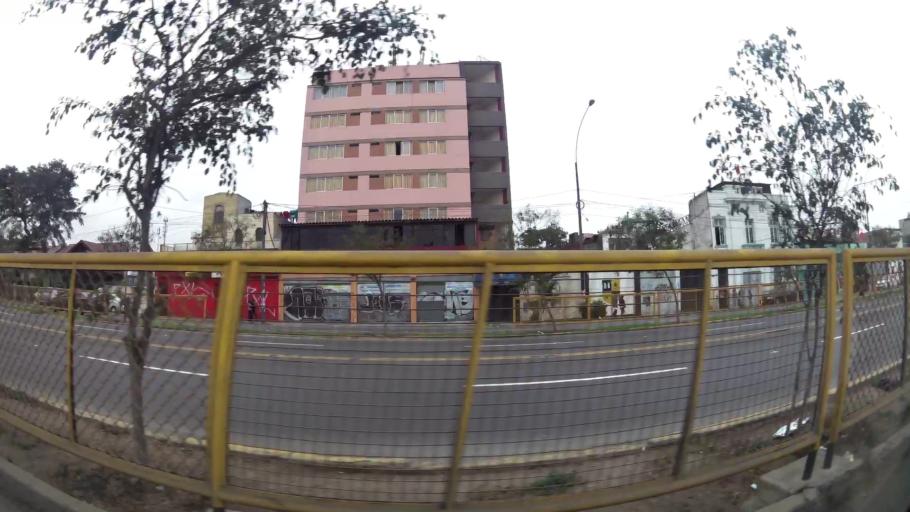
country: PE
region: Lima
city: Lima
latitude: -12.0643
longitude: -77.0451
